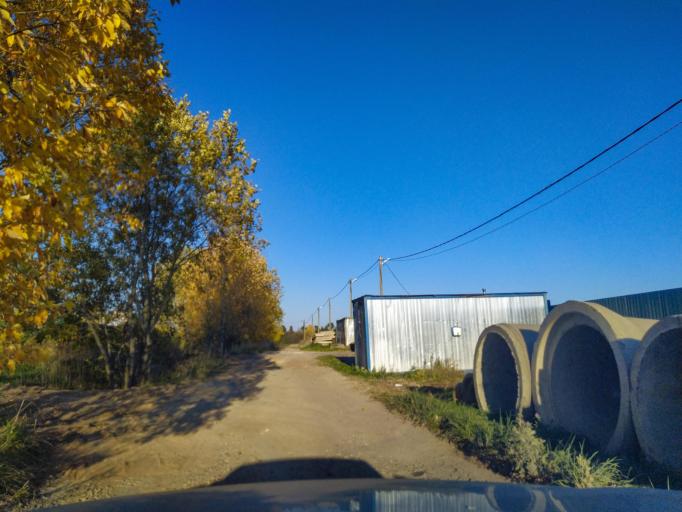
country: RU
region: Leningrad
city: Siverskiy
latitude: 59.3219
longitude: 30.0452
